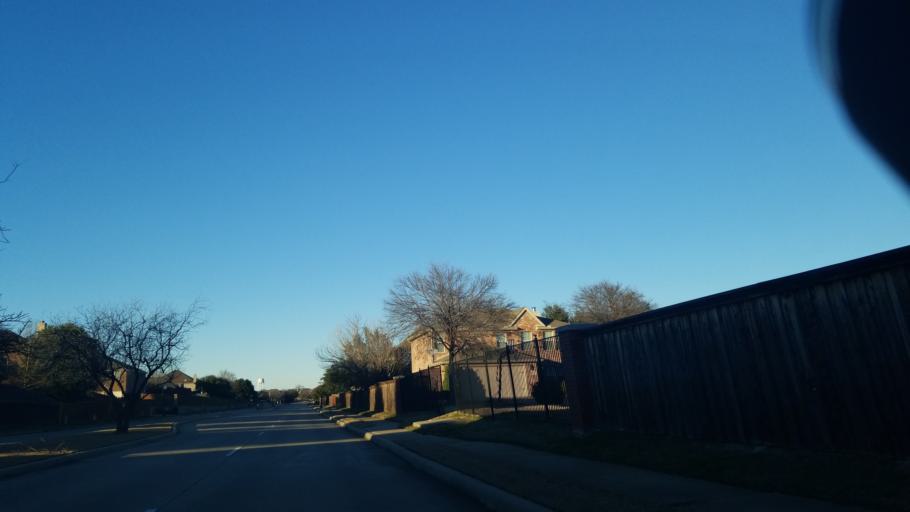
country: US
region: Texas
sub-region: Denton County
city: Shady Shores
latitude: 33.1464
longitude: -97.0426
